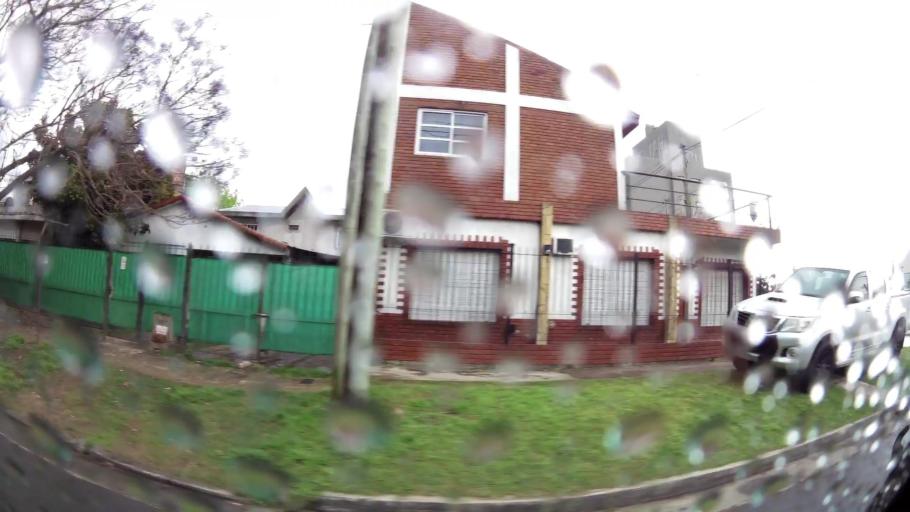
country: AR
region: Buenos Aires
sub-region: Partido de Quilmes
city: Quilmes
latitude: -34.7726
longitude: -58.2271
